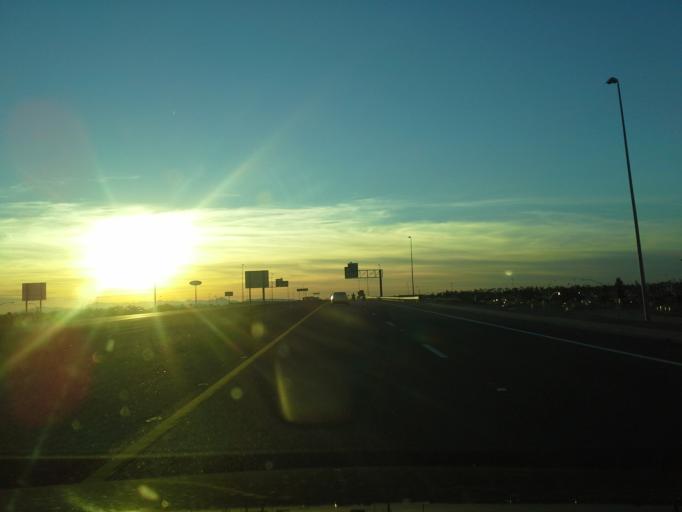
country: US
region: Arizona
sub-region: Pinal County
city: Apache Junction
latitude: 33.3867
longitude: -111.5262
